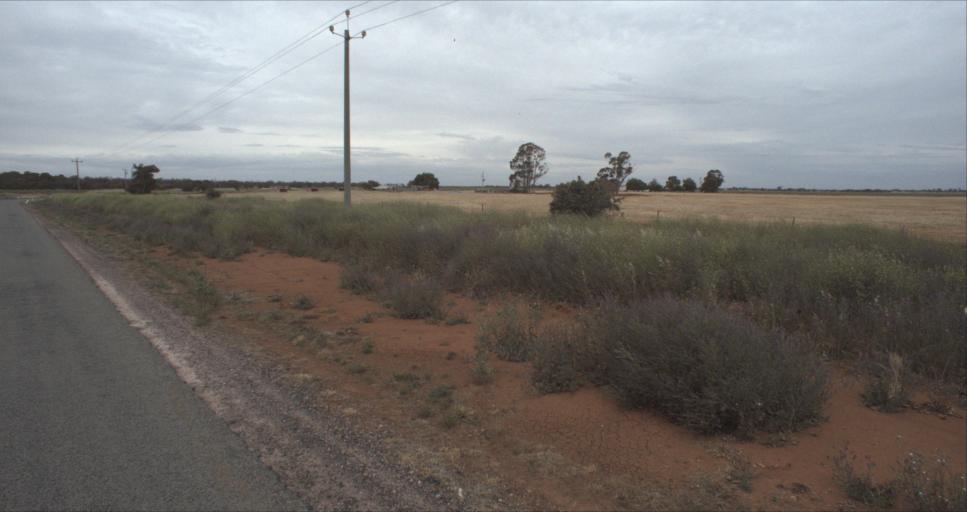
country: AU
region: New South Wales
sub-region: Leeton
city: Leeton
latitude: -34.4484
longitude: 146.3858
